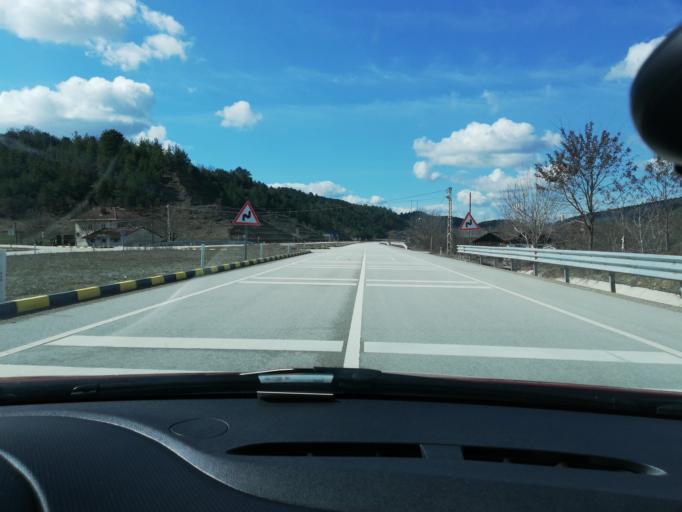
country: TR
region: Kastamonu
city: Igdir
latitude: 41.2330
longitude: 33.0463
